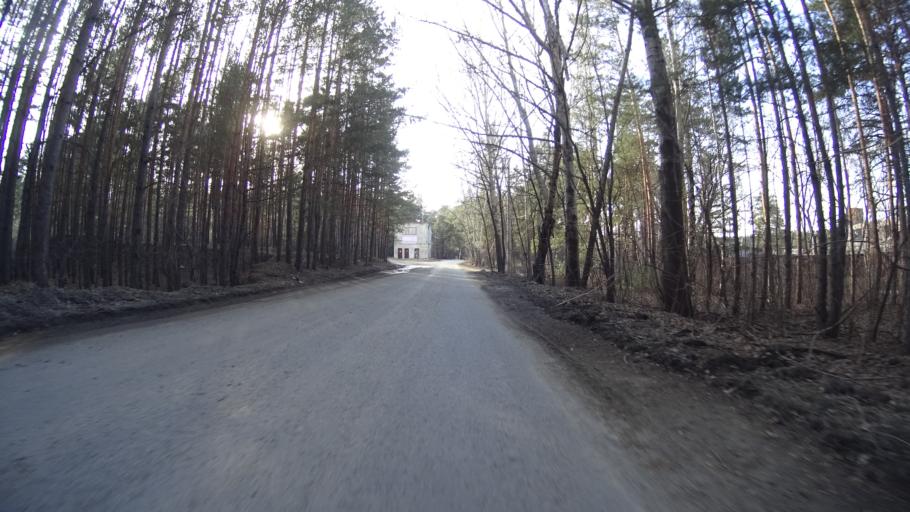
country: RU
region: Chelyabinsk
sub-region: Gorod Chelyabinsk
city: Chelyabinsk
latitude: 55.1282
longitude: 61.3591
